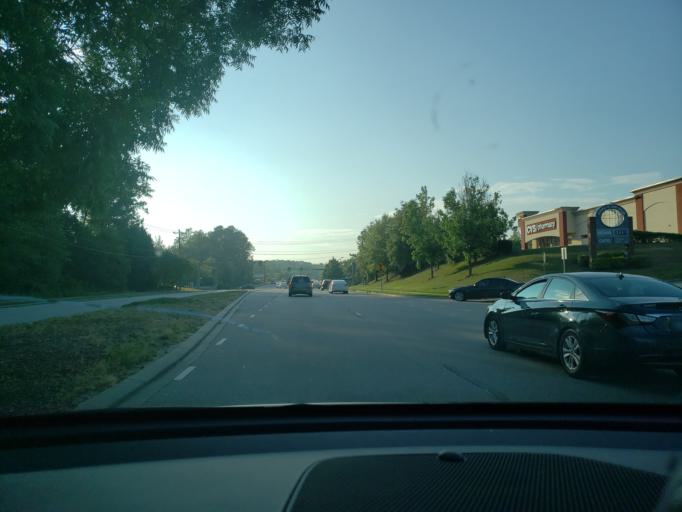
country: US
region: North Carolina
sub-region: Durham County
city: Durham
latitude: 35.9470
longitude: -78.9228
